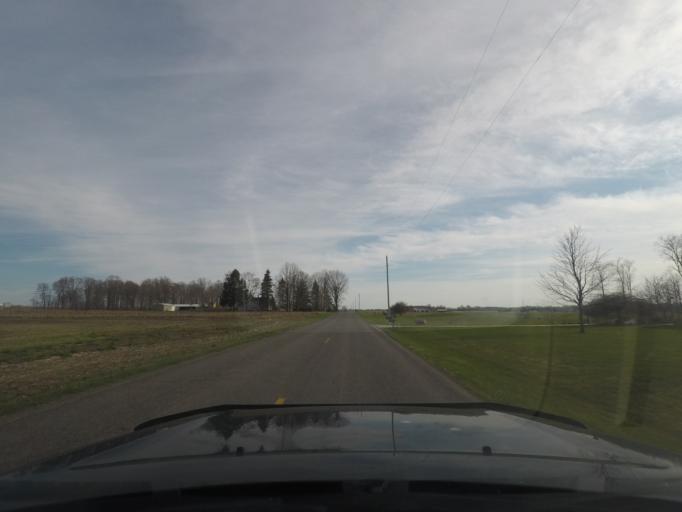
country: US
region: Indiana
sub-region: Elkhart County
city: Dunlap
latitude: 41.5726
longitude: -85.9250
